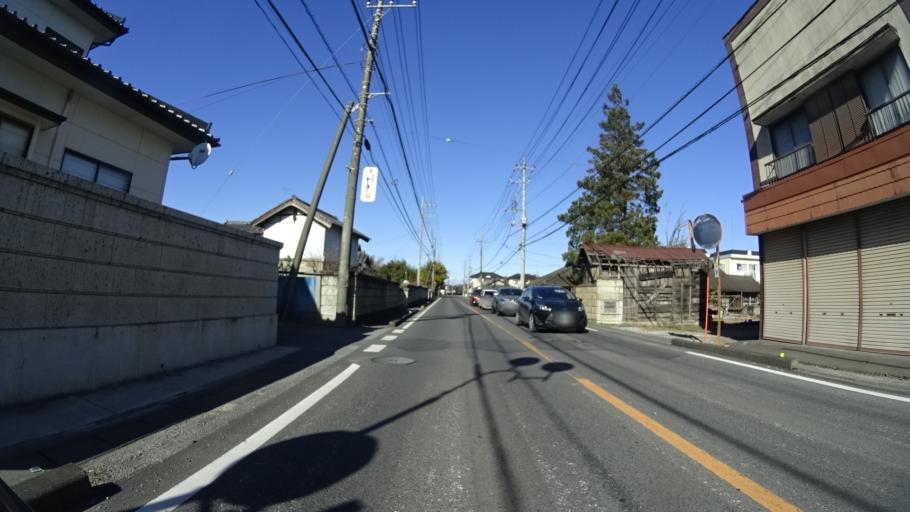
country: JP
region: Tochigi
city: Tochigi
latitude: 36.4294
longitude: 139.7492
